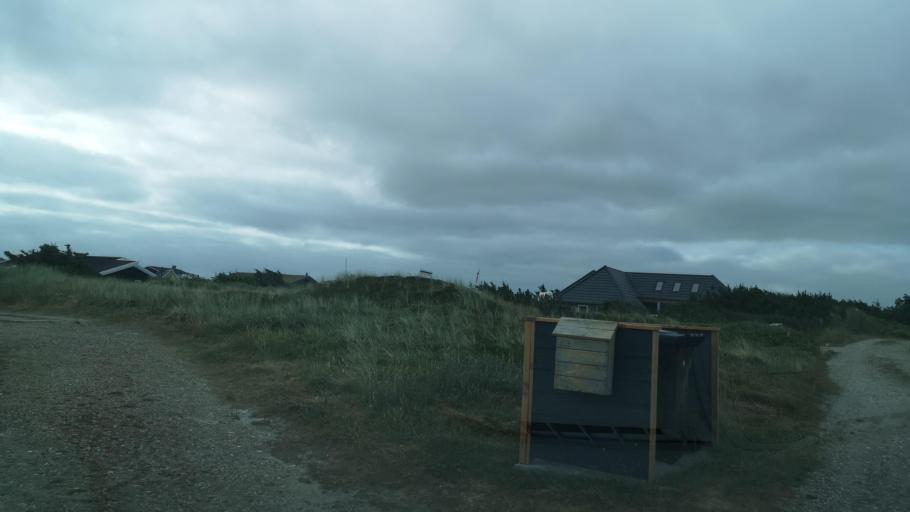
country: DK
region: Central Jutland
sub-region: Ringkobing-Skjern Kommune
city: Ringkobing
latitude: 56.1422
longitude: 8.1182
